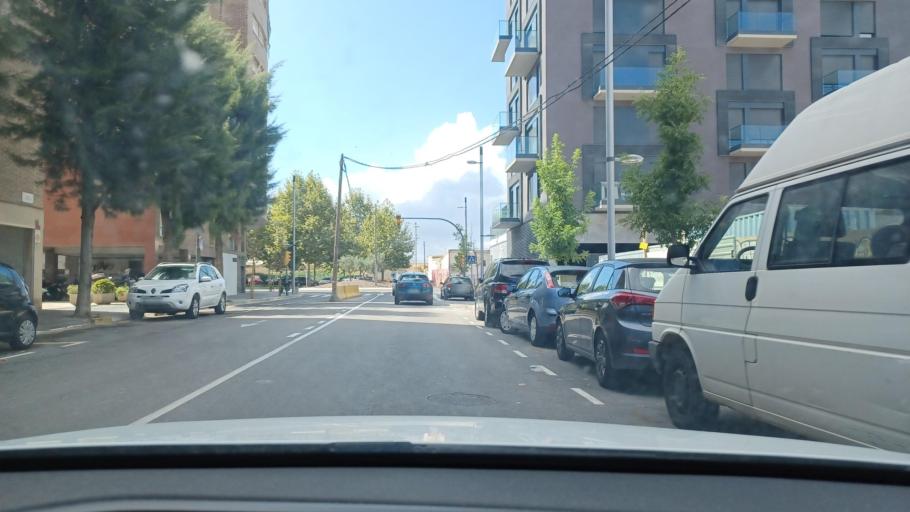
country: ES
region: Catalonia
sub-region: Provincia de Tarragona
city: Tarragona
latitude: 41.1125
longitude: 1.2398
